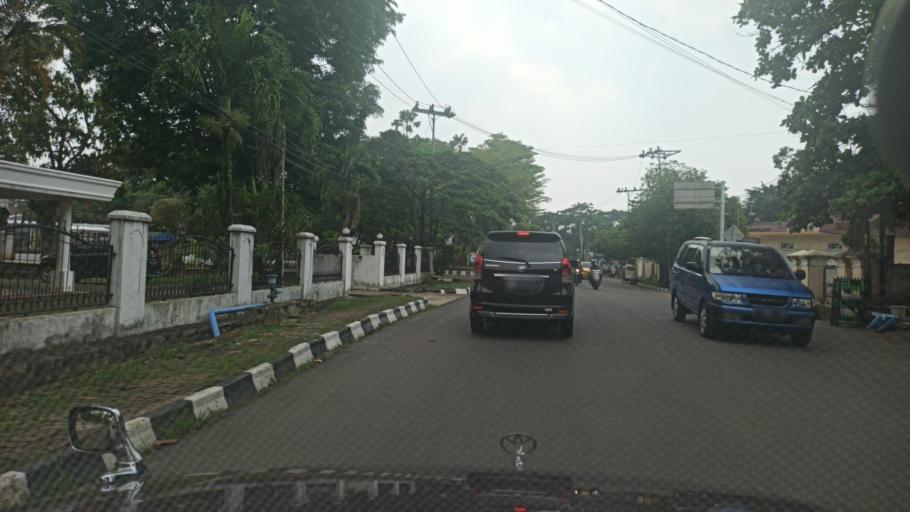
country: ID
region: South Sumatra
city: Plaju
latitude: -2.9911
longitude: 104.7497
